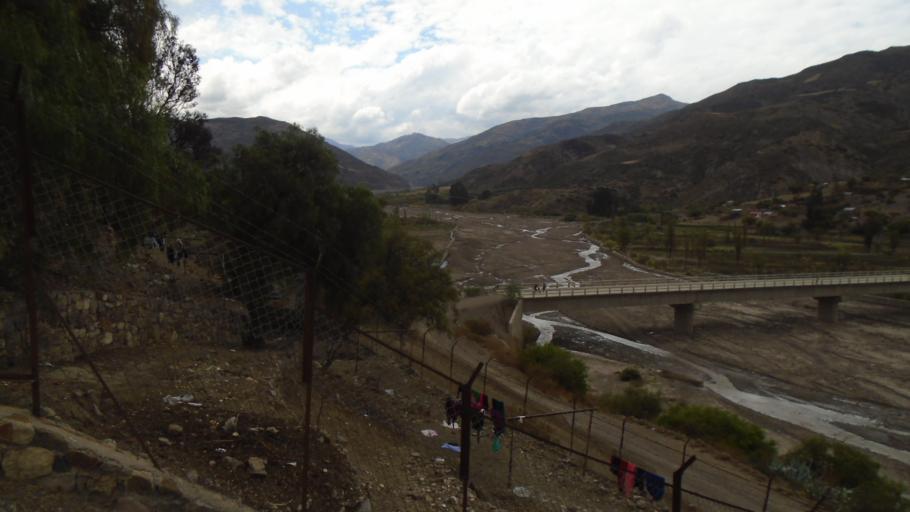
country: BO
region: Cochabamba
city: Colchani
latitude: -17.5165
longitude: -66.6182
